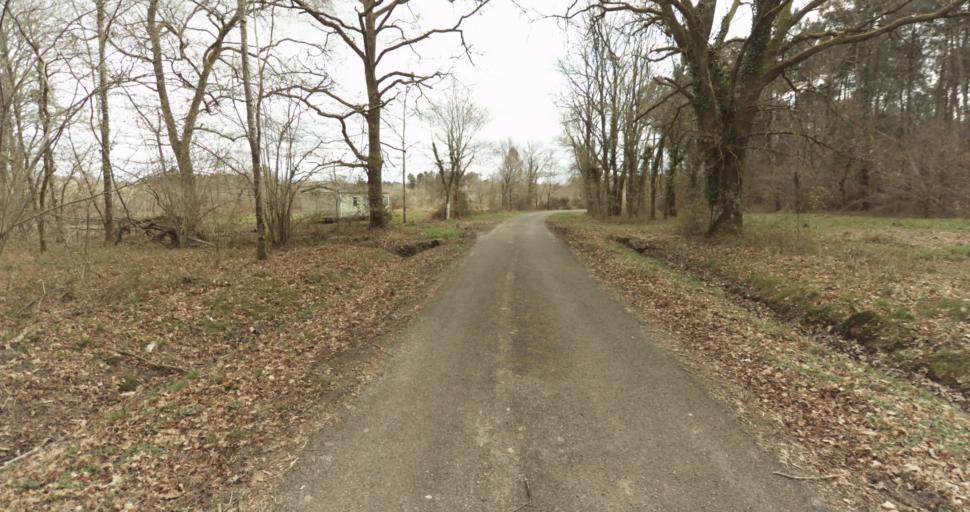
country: FR
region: Aquitaine
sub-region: Departement des Landes
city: Roquefort
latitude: 44.0770
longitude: -0.3995
